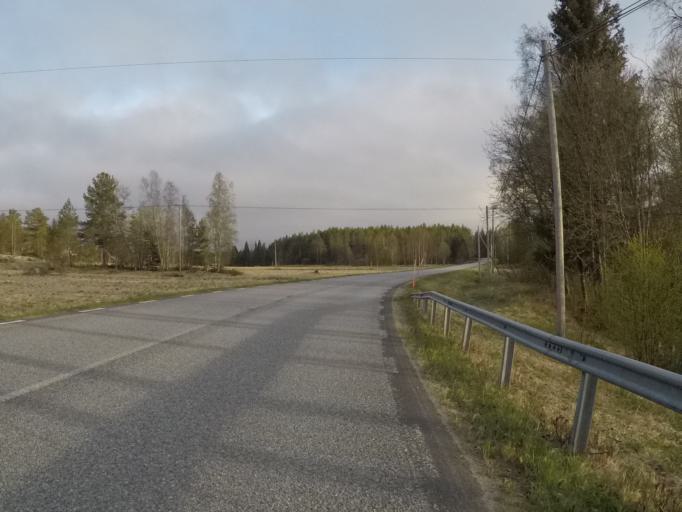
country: SE
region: Vaesterbotten
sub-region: Robertsfors Kommun
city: Robertsfors
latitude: 63.9666
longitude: 20.8121
